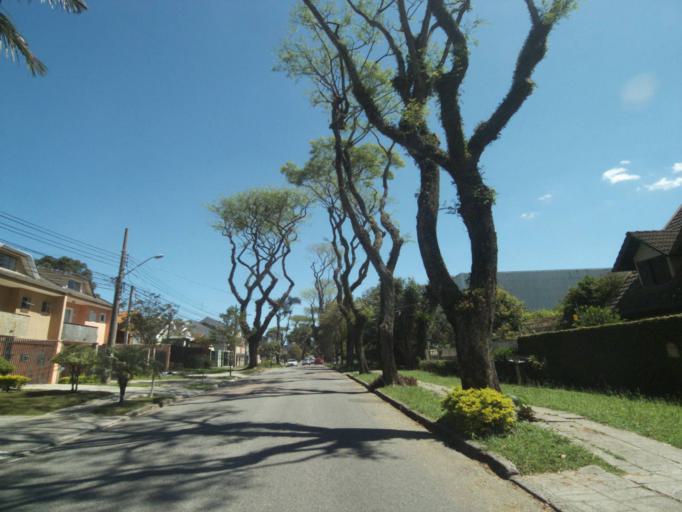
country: BR
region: Parana
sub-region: Curitiba
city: Curitiba
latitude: -25.3918
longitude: -49.2418
